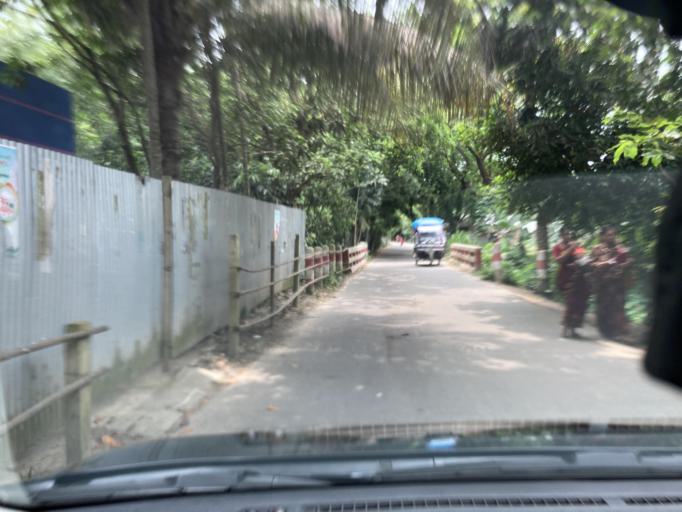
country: BD
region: Dhaka
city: Dohar
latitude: 23.8103
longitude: 90.0456
